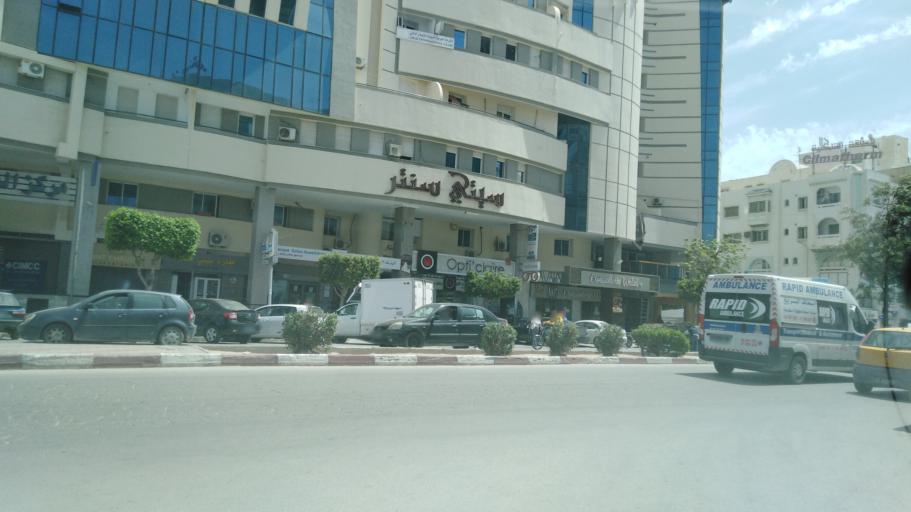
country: TN
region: Safaqis
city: Sfax
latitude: 34.7427
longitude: 10.7543
